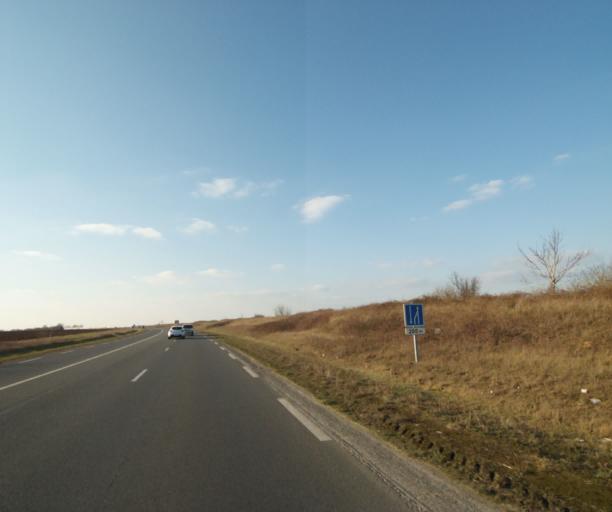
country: FR
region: Poitou-Charentes
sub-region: Departement des Deux-Sevres
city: Vouille
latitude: 46.3143
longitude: -0.3829
